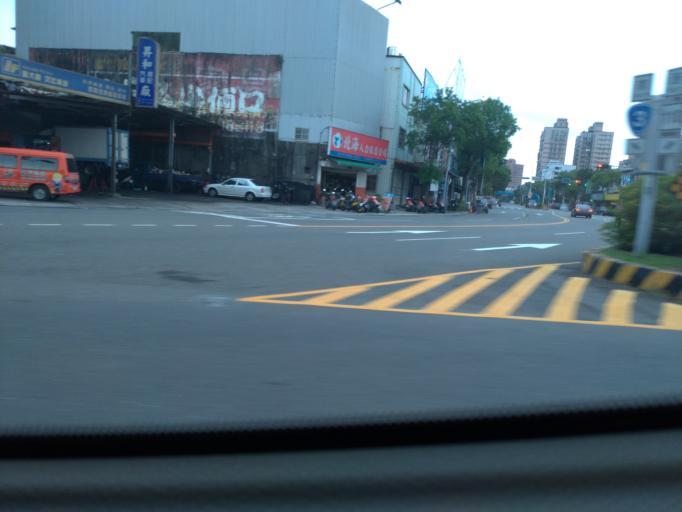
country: TW
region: Taiwan
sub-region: Taoyuan
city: Taoyuan
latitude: 24.9313
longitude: 121.3766
